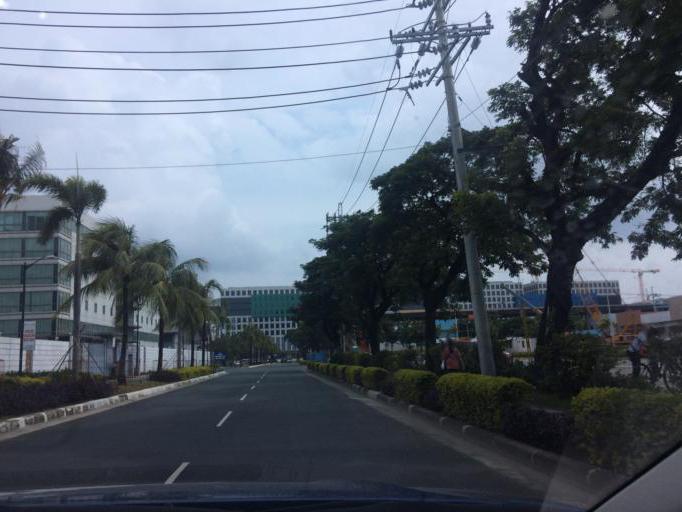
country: PH
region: Metro Manila
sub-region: Makati City
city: Makati City
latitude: 14.5395
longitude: 120.9906
